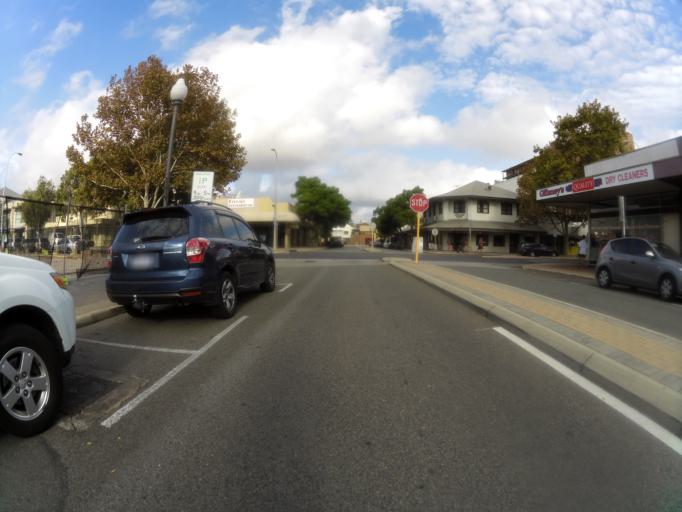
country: AU
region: Western Australia
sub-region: Fremantle
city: Fremantle
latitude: -32.0517
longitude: 115.7486
